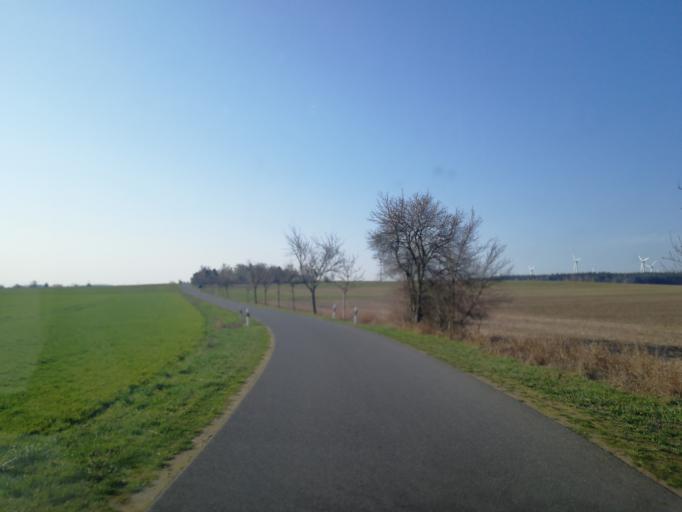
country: DE
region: Brandenburg
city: Drahnsdorf
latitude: 51.8841
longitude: 13.5836
